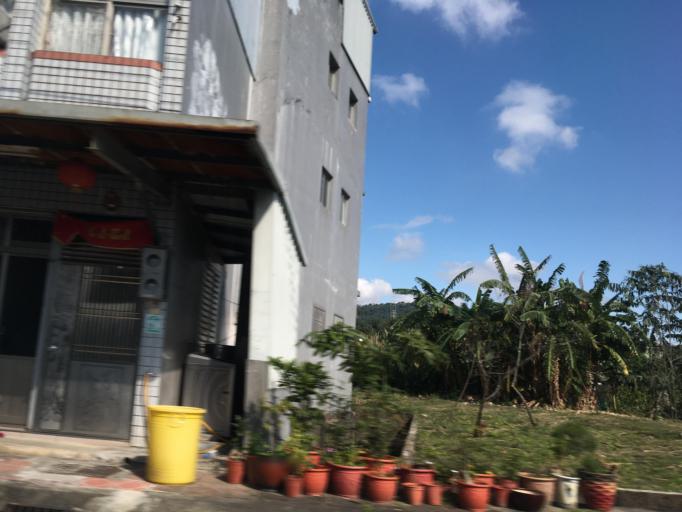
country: TW
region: Taiwan
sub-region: Yilan
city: Yilan
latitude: 24.7454
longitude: 121.6982
